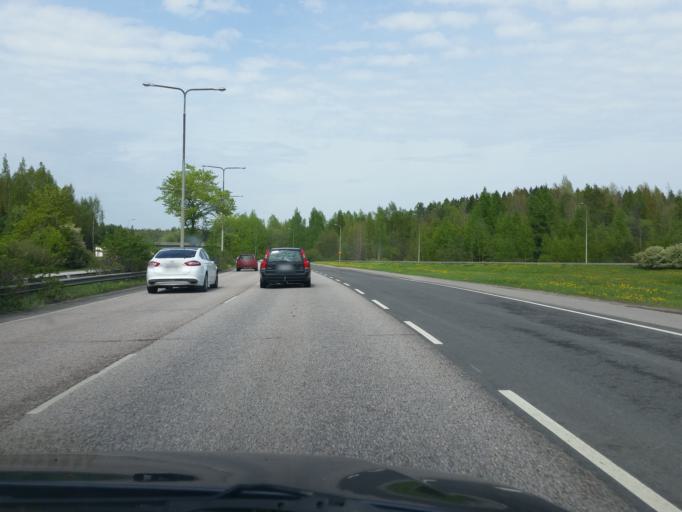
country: FI
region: Uusimaa
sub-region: Helsinki
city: Helsinki
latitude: 60.2202
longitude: 24.9096
